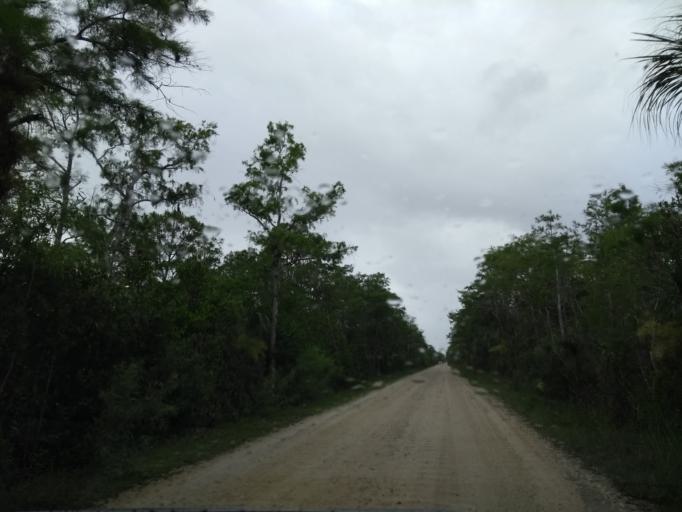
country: US
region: Florida
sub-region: Miami-Dade County
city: The Hammocks
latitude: 25.7605
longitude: -80.9991
